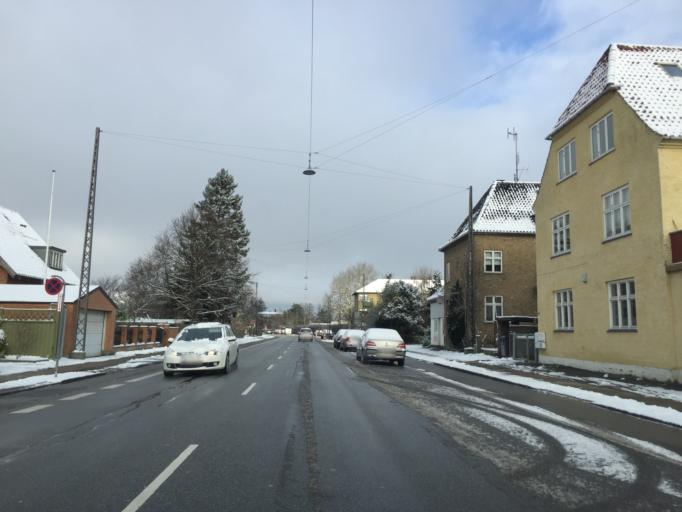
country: DK
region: Capital Region
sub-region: Tarnby Kommune
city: Tarnby
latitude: 55.6506
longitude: 12.6262
